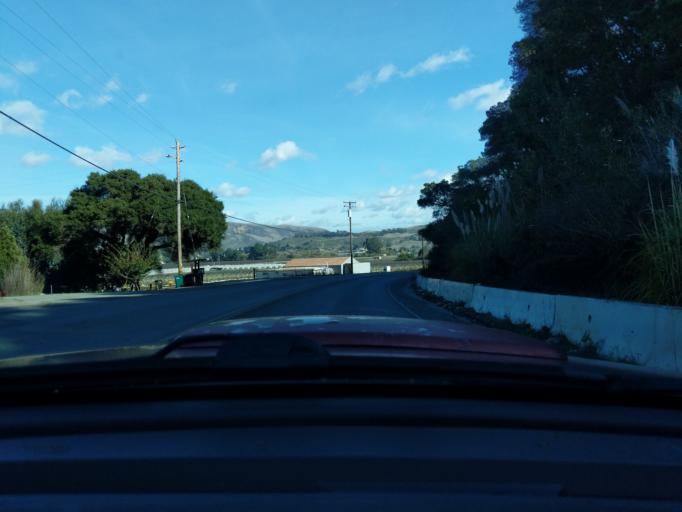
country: US
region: California
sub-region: San Benito County
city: Aromas
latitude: 36.8866
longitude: -121.6561
